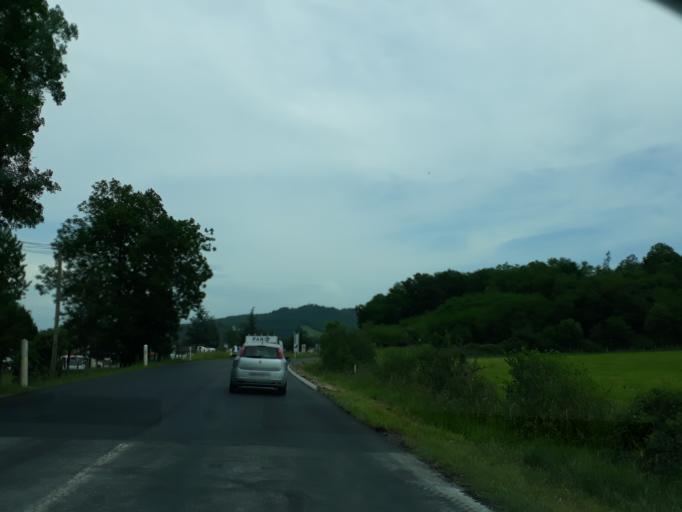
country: FR
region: Limousin
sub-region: Departement de la Correze
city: Larche
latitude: 45.1251
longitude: 1.4003
